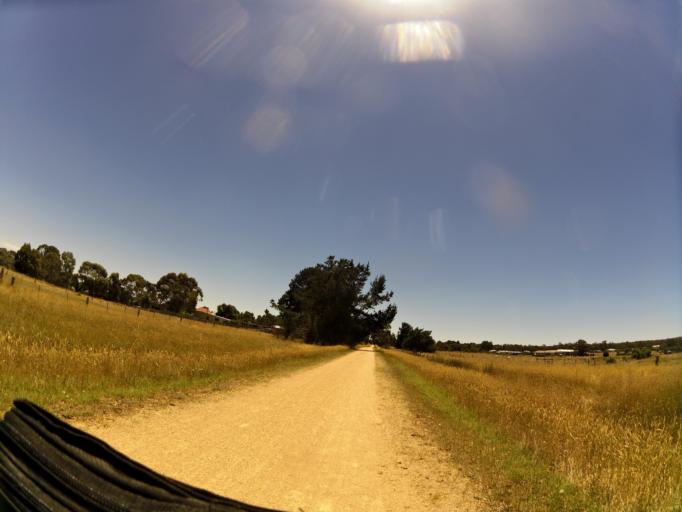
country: AU
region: Victoria
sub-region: Ballarat North
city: Delacombe
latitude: -37.5980
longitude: 143.7188
